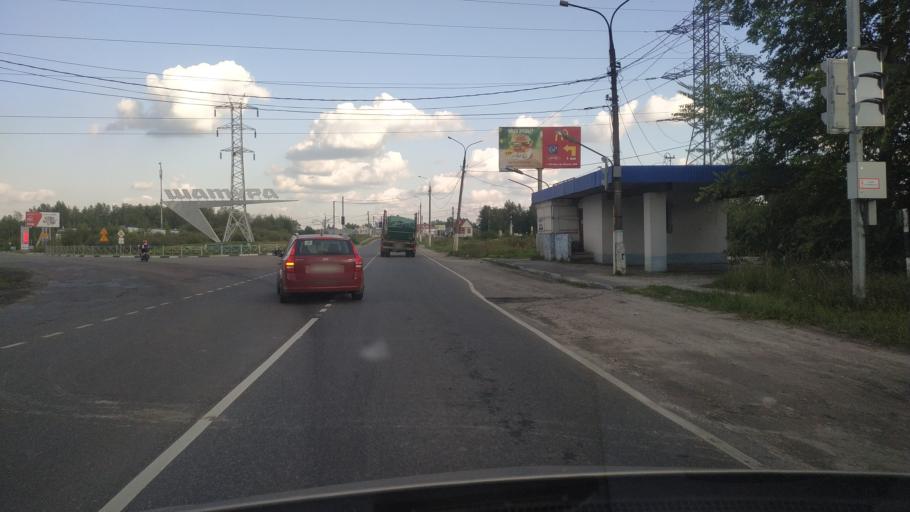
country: RU
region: Moskovskaya
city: Shatura
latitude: 55.5758
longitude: 39.4993
